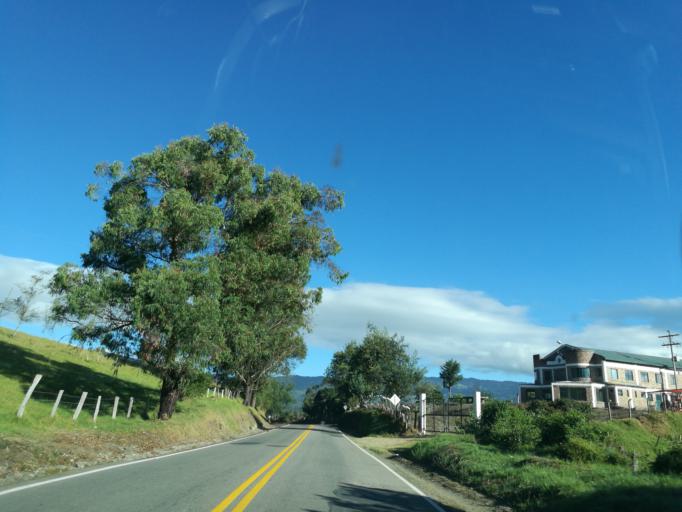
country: CO
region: Boyaca
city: Chiquinquira
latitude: 5.6272
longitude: -73.7894
